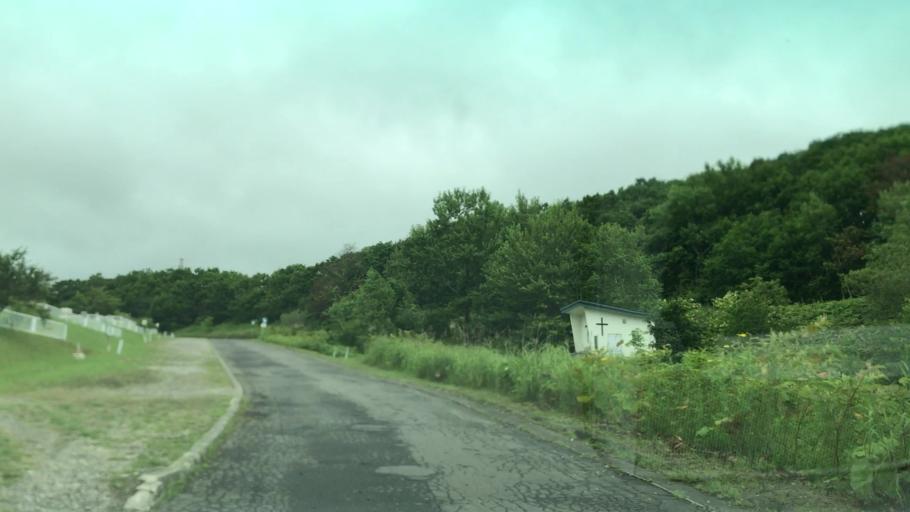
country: JP
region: Hokkaido
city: Muroran
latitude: 42.3954
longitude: 141.0009
